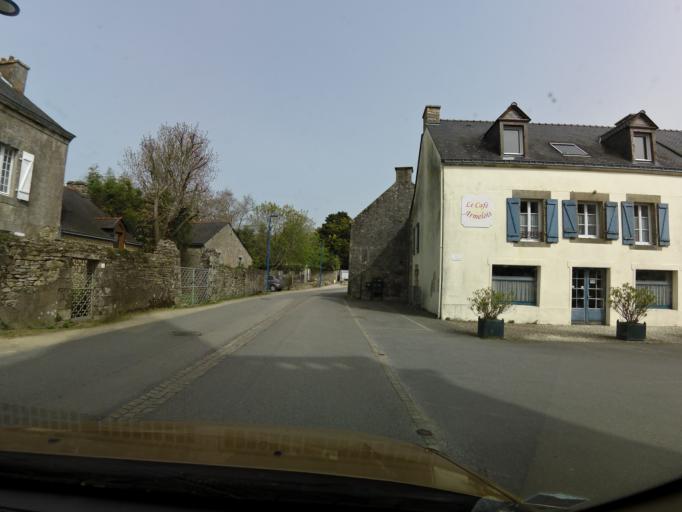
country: FR
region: Brittany
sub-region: Departement du Morbihan
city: Sene
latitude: 47.5731
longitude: -2.7097
